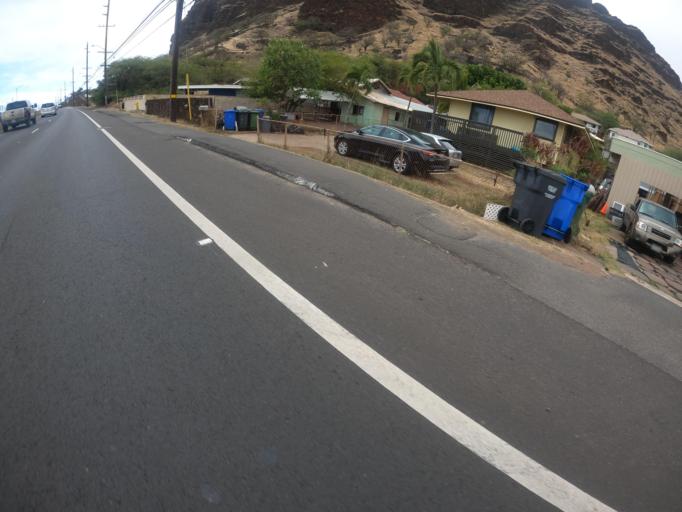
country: US
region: Hawaii
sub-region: Honolulu County
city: Nanakuli
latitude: 21.3978
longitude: -158.1663
